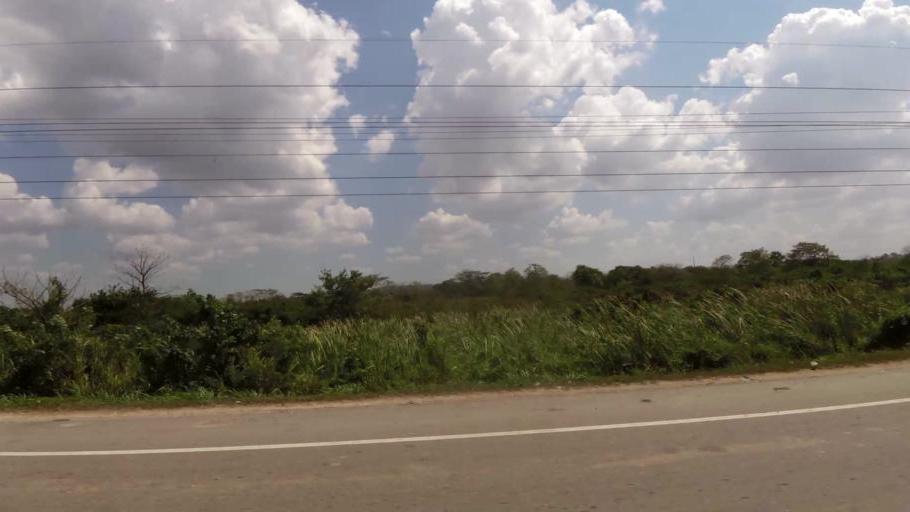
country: CO
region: Bolivar
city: Cartagena
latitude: 10.3473
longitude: -75.4831
